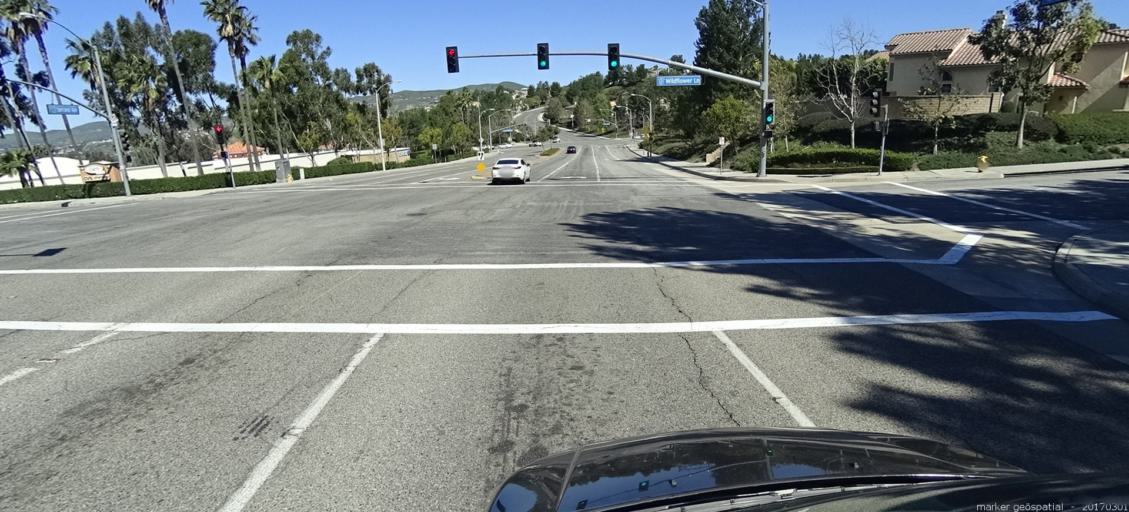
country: US
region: California
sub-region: Orange County
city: Yorba Linda
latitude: 33.8601
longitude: -117.7373
